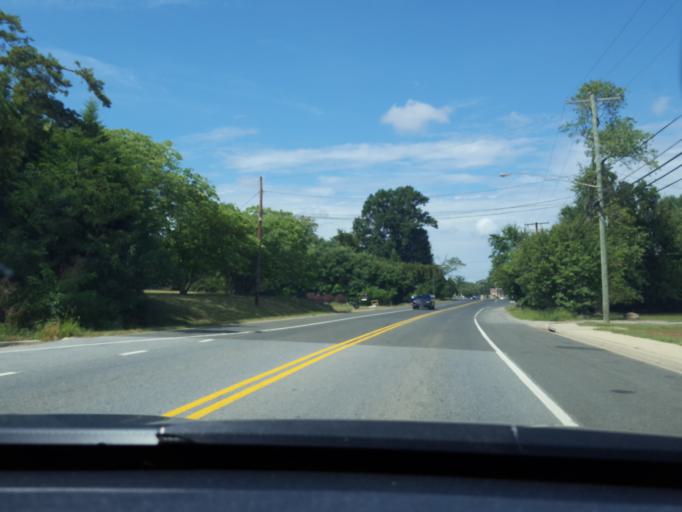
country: US
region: Maryland
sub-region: Prince George's County
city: Andrews AFB
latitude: 38.7779
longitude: -76.8710
